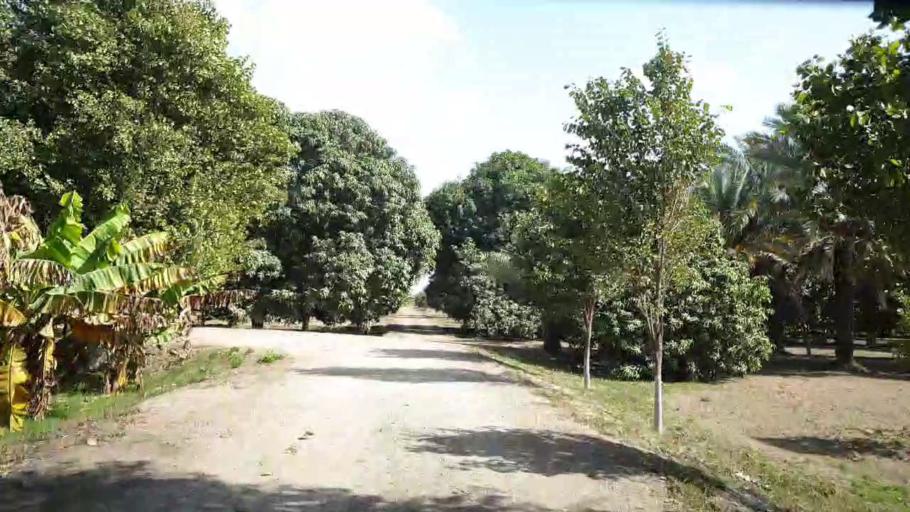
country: PK
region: Sindh
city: Tando Jam
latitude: 25.5370
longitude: 68.5737
